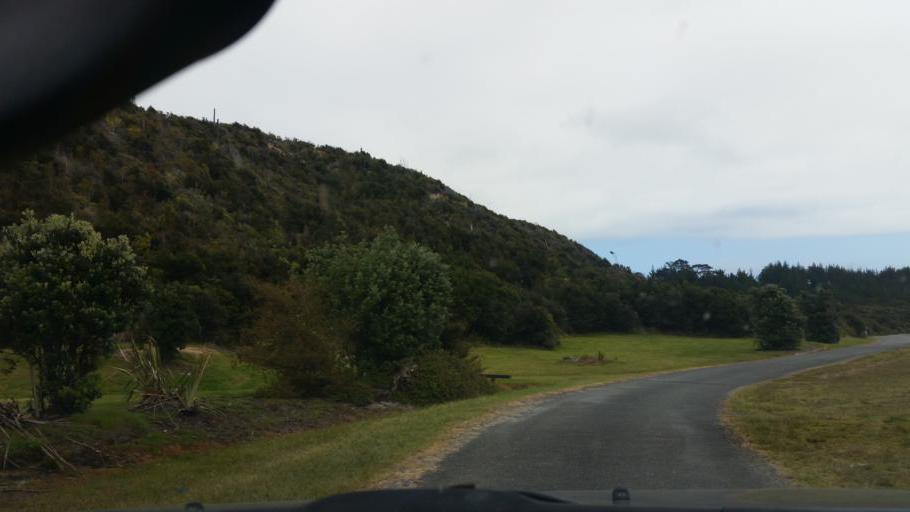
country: NZ
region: Northland
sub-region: Kaipara District
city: Dargaville
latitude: -35.8102
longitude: 173.6626
